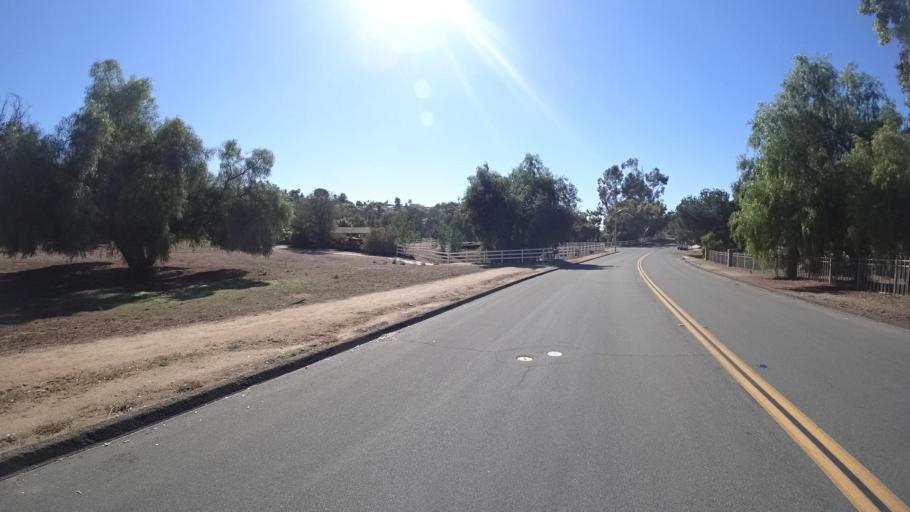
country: US
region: California
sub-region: San Diego County
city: Harbison Canyon
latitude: 32.8653
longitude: -116.8643
